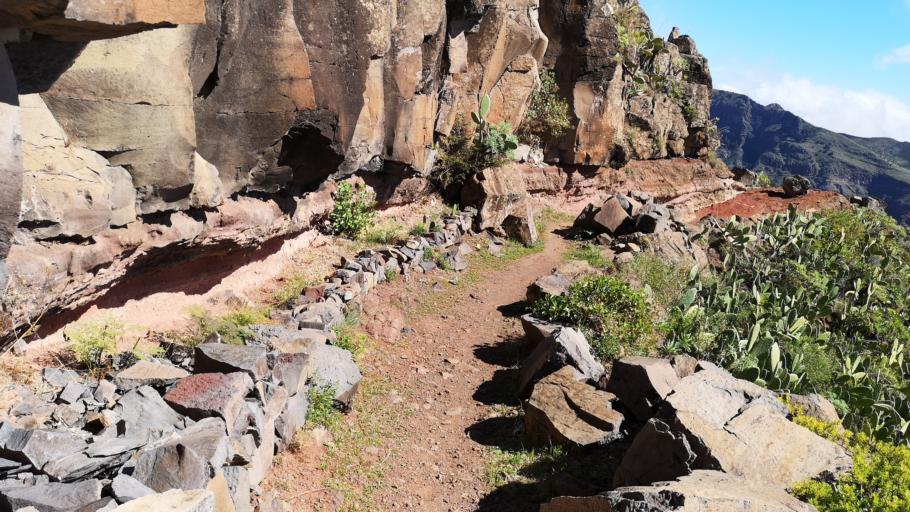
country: ES
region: Canary Islands
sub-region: Provincia de Santa Cruz de Tenerife
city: Alajero
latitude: 28.0836
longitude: -17.2324
